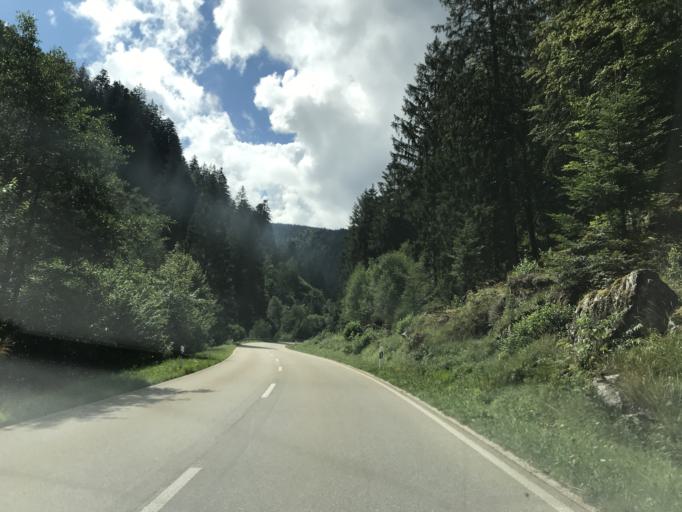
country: DE
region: Baden-Wuerttemberg
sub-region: Freiburg Region
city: Oberried
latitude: 47.9145
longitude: 7.9343
